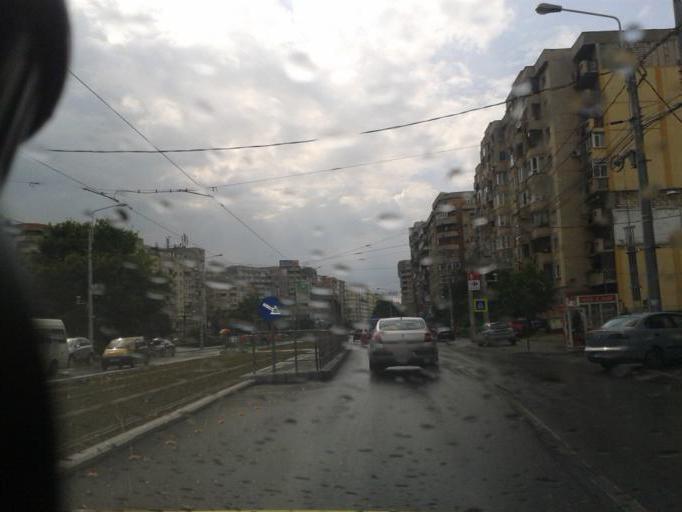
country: RO
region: Prahova
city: Ploiesti
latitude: 44.9475
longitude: 26.0124
